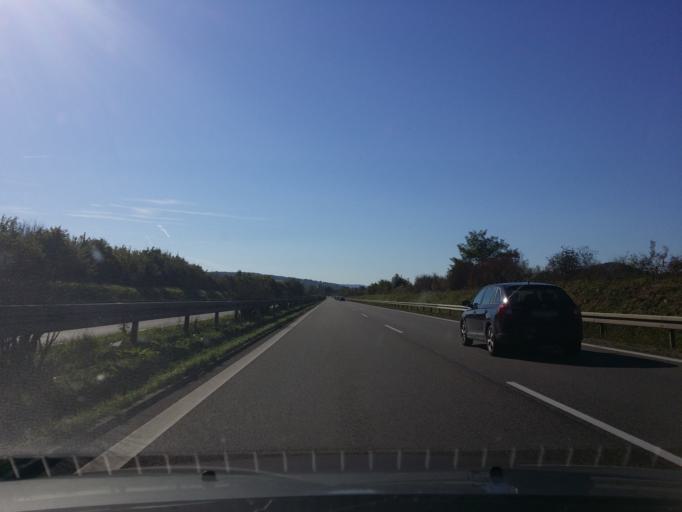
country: DE
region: Baden-Wuerttemberg
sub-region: Tuebingen Region
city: Kusterdingen
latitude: 48.5289
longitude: 9.1047
